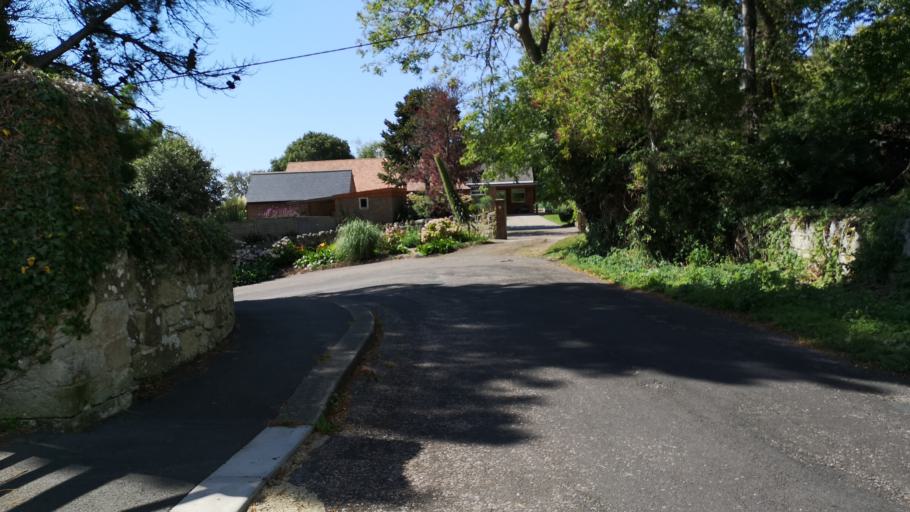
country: GB
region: England
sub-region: Isle of Wight
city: Ventnor
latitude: 50.5906
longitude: -1.2314
